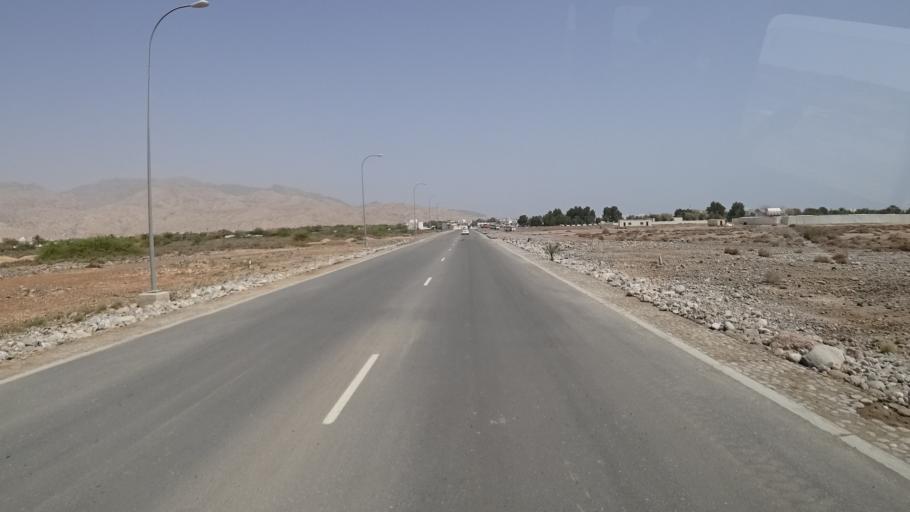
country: OM
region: Muhafazat Masqat
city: Muscat
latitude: 23.2506
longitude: 58.9110
